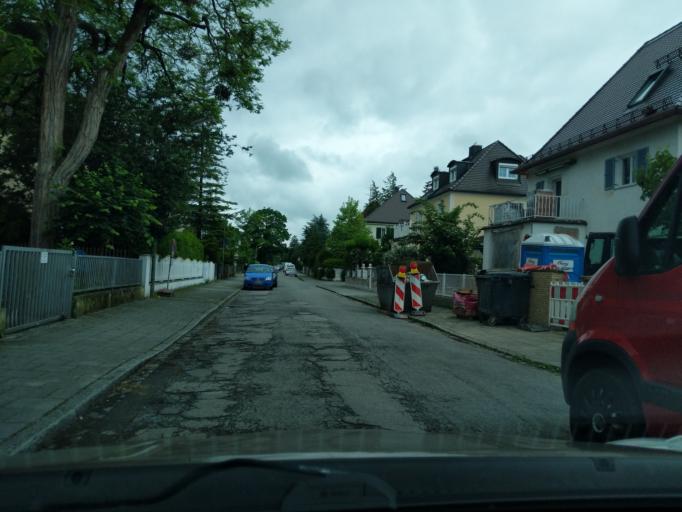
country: DE
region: Bavaria
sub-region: Upper Bavaria
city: Pullach im Isartal
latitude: 48.1116
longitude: 11.5136
